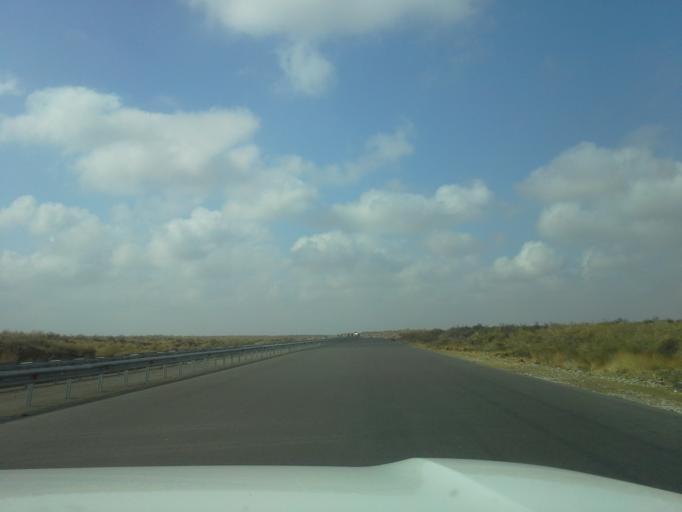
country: TM
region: Mary
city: Mary
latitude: 37.3833
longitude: 61.4880
